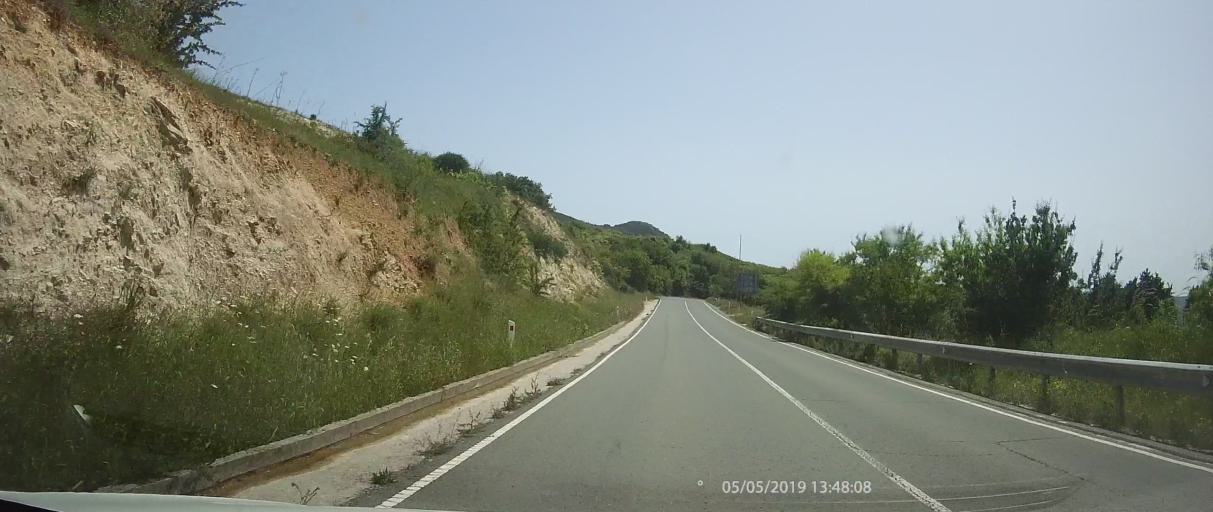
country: CY
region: Limassol
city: Pachna
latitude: 34.8600
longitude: 32.7560
